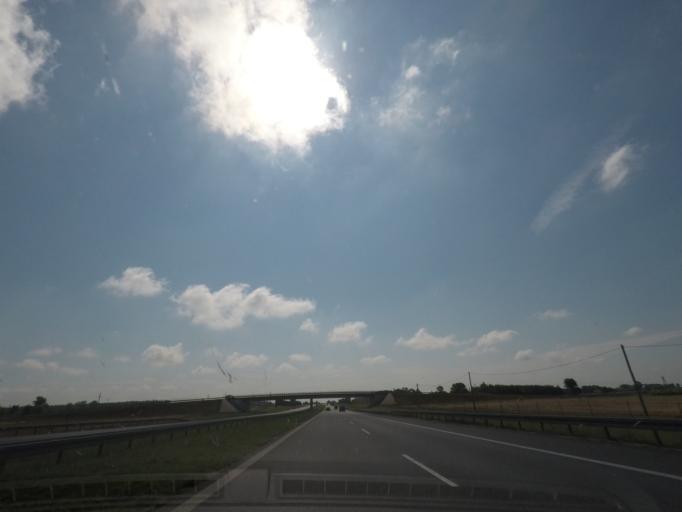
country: PL
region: Kujawsko-Pomorskie
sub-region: Powiat wloclawski
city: Baruchowo
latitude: 52.4507
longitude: 19.2219
